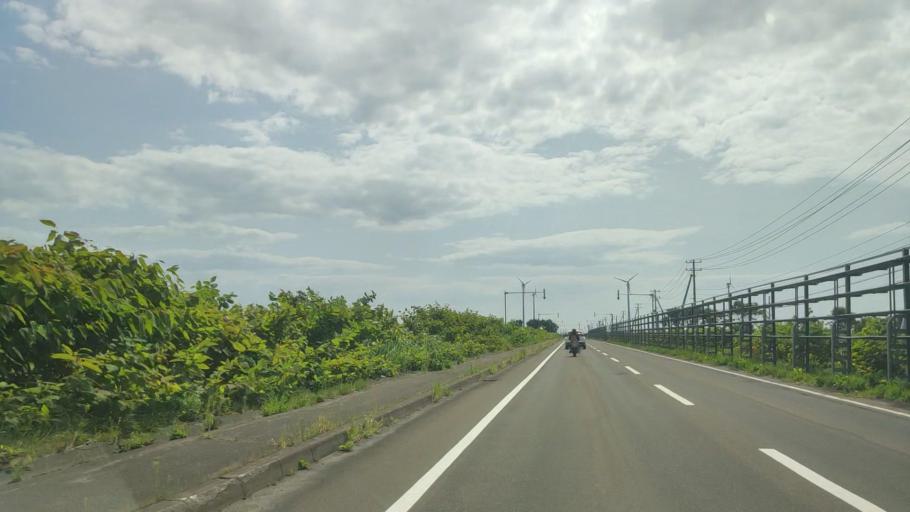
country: JP
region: Hokkaido
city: Rumoi
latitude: 44.3938
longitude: 141.7179
